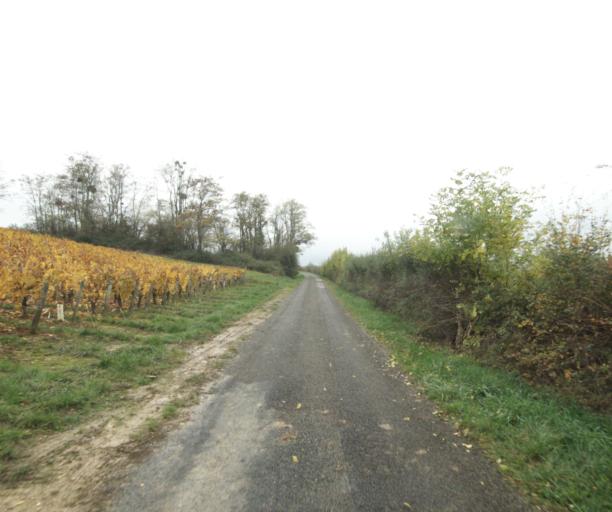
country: FR
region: Rhone-Alpes
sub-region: Departement de l'Ain
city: Pont-de-Vaux
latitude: 46.4716
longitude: 4.8787
